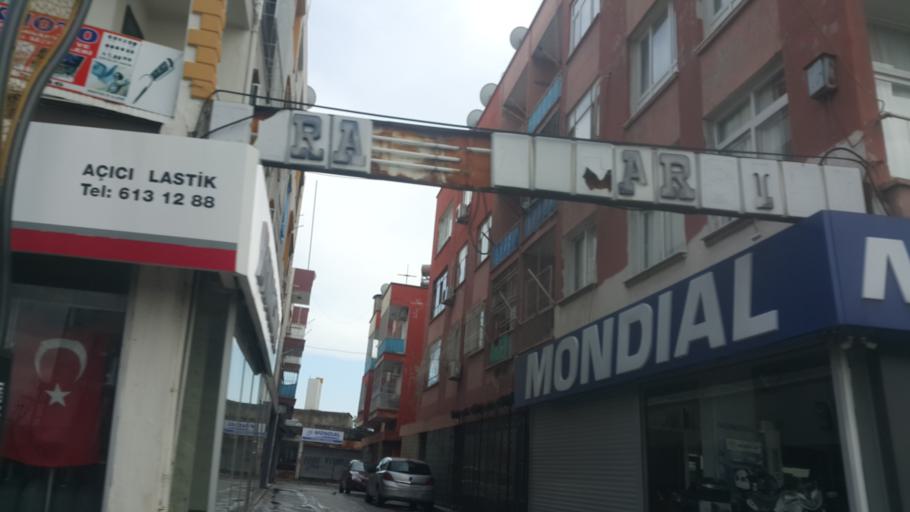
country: TR
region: Mersin
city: Tarsus
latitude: 36.9196
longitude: 34.9029
